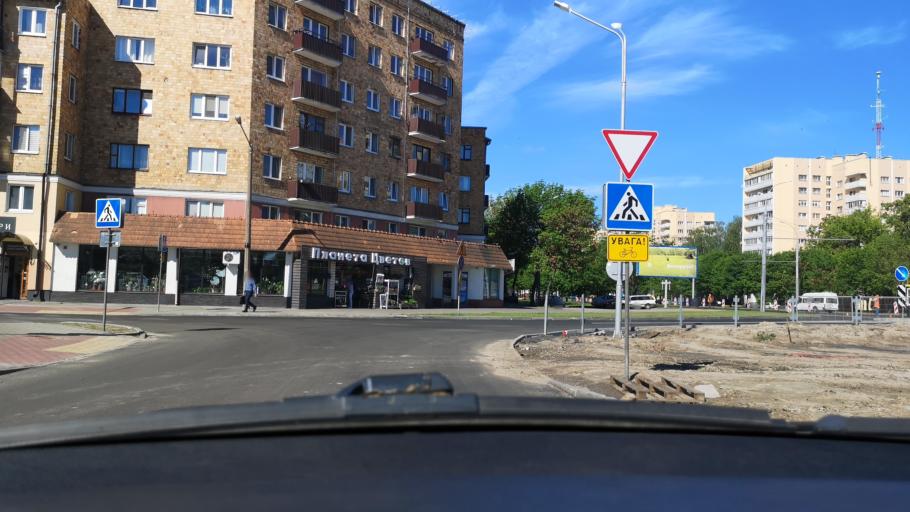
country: BY
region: Brest
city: Brest
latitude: 52.0892
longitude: 23.7124
